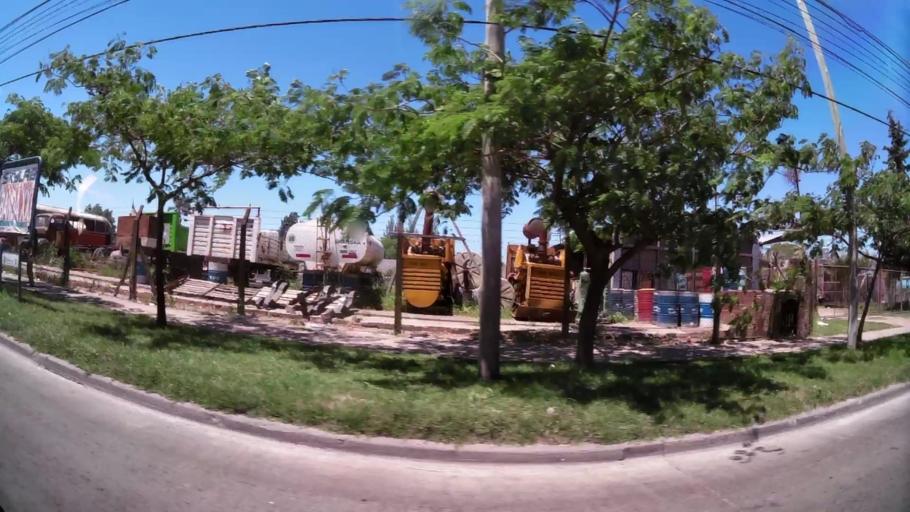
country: AR
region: Buenos Aires
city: Hurlingham
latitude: -34.5006
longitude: -58.7118
